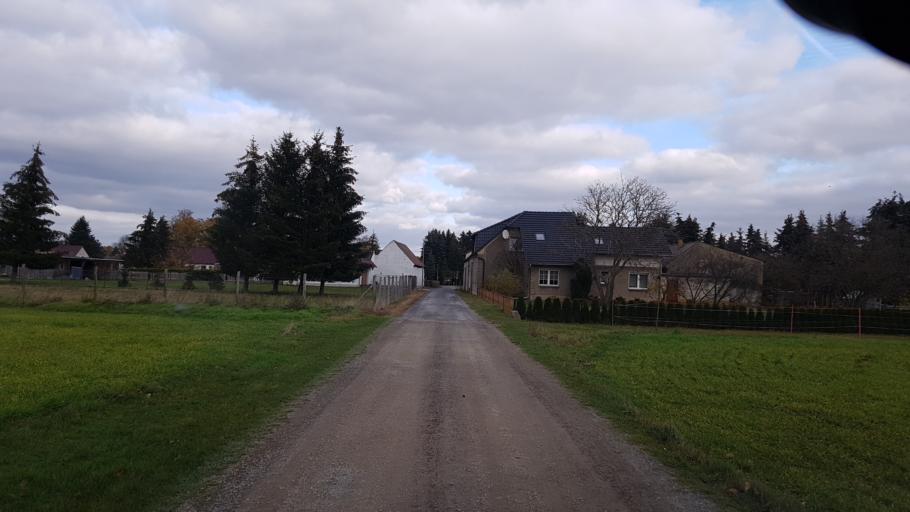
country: DE
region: Brandenburg
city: Sallgast
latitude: 51.6045
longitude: 13.8591
